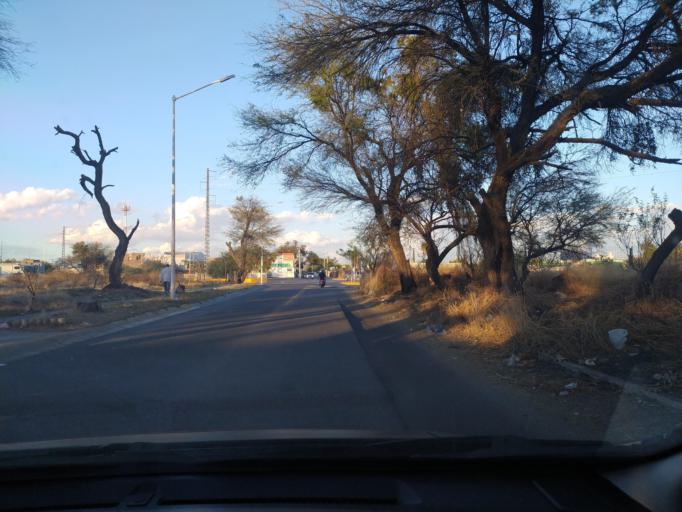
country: LA
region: Oudomxai
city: Muang La
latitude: 21.0074
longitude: 101.8705
